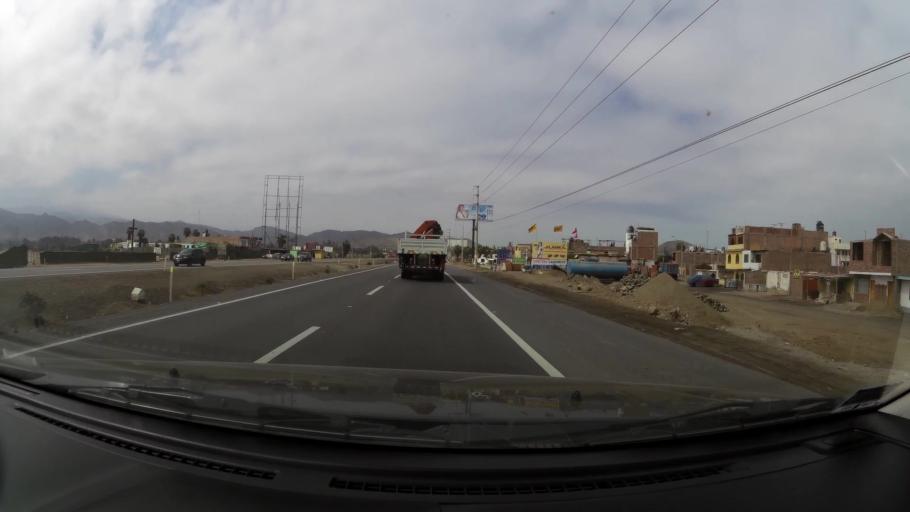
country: PE
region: Lima
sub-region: Provincia de Canete
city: Mala
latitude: -12.7100
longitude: -76.6331
